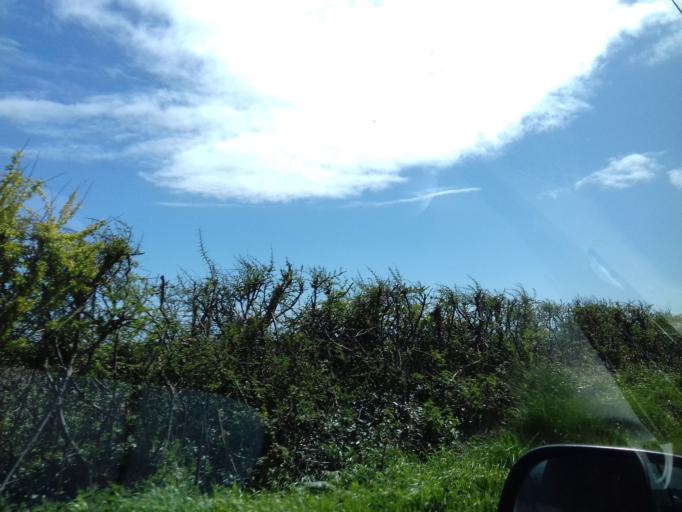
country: IE
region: Munster
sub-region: Waterford
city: Dunmore East
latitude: 52.2190
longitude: -6.8602
